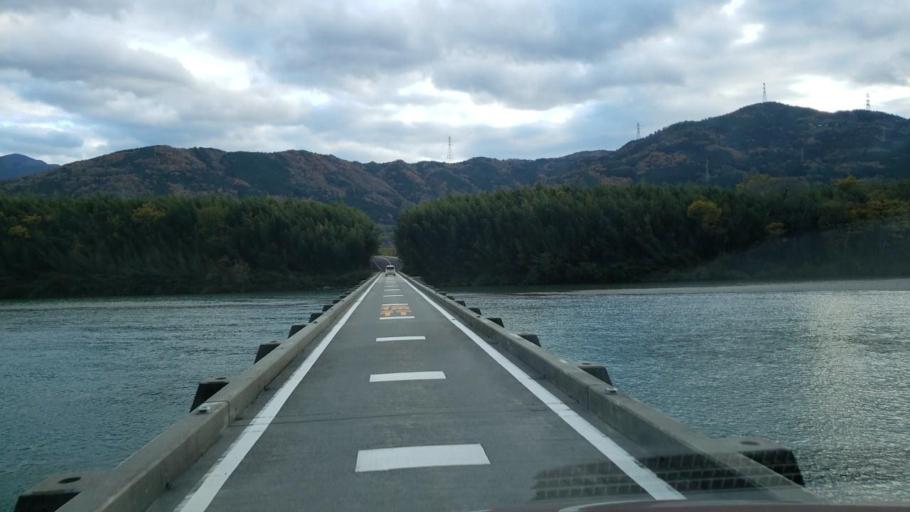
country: JP
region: Tokushima
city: Wakimachi
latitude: 34.0655
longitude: 134.1431
